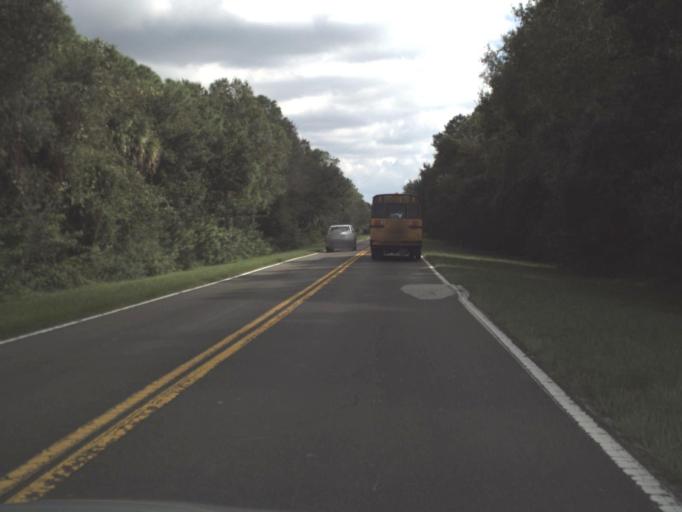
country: US
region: Florida
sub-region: Sarasota County
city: Plantation
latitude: 27.0656
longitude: -82.3199
